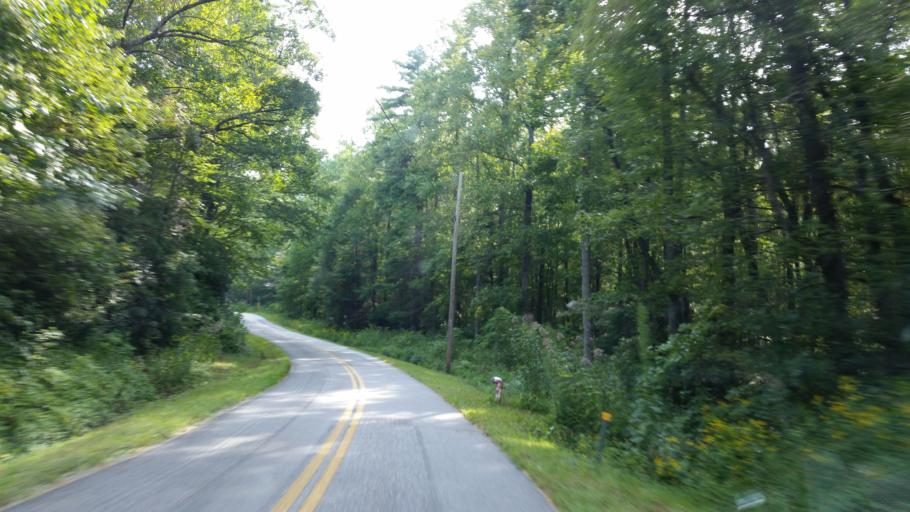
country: US
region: Georgia
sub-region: Lumpkin County
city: Dahlonega
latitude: 34.6752
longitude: -84.0280
